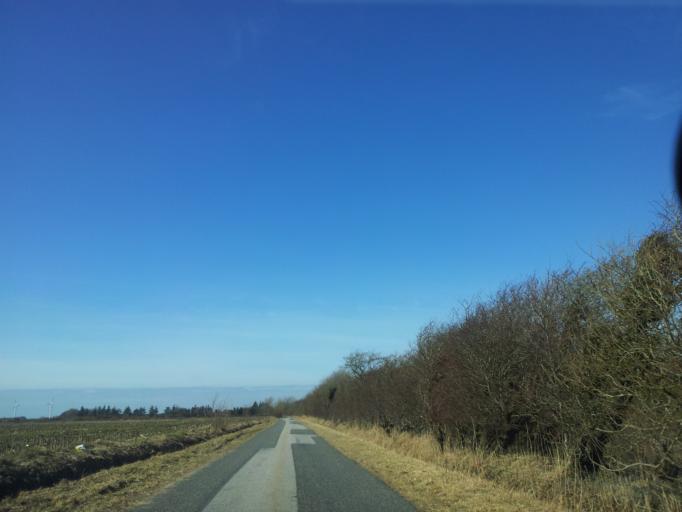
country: DK
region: South Denmark
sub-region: Tonder Kommune
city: Sherrebek
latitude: 55.2039
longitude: 8.7431
